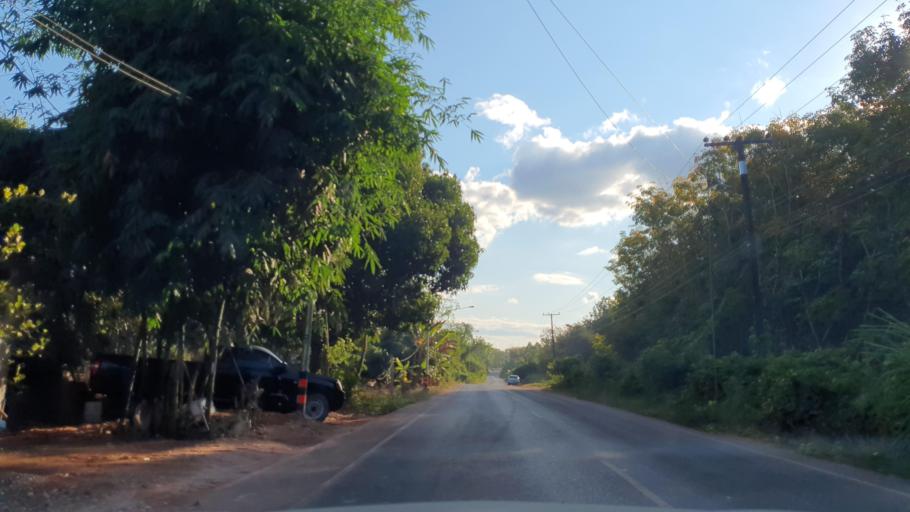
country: TH
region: Changwat Bueng Kan
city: Si Wilai
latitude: 18.1474
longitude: 103.8977
